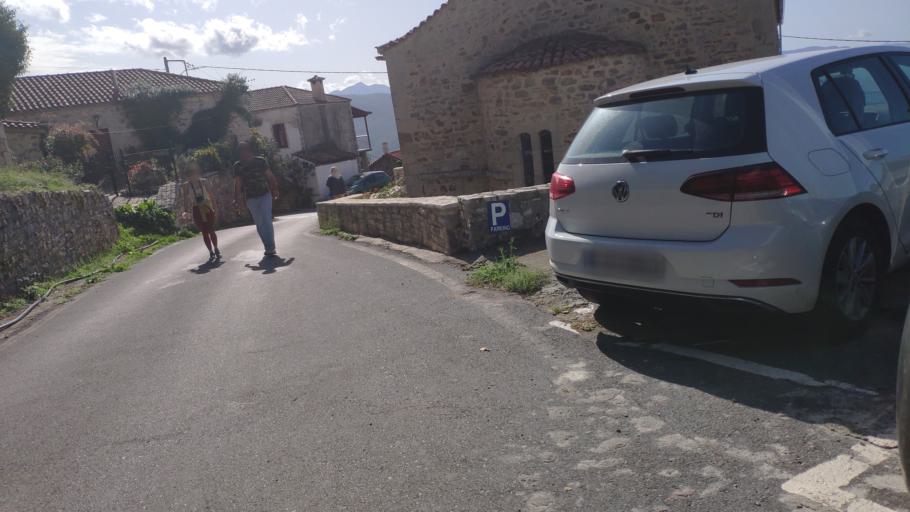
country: GR
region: Peloponnese
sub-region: Nomos Arkadias
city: Dimitsana
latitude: 37.5596
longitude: 21.9909
